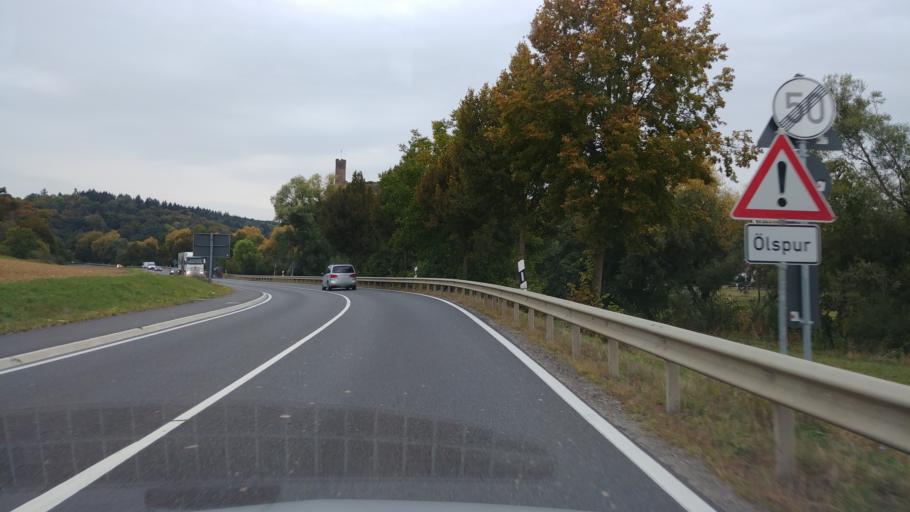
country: DE
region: Rheinland-Pfalz
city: Holzheim
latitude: 50.3520
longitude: 8.0460
